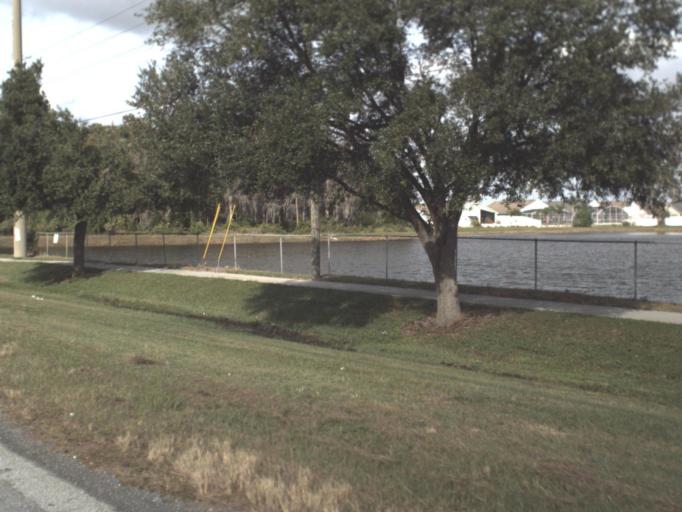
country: US
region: Florida
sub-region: Orange County
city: Williamsburg
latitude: 28.4053
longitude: -81.4250
